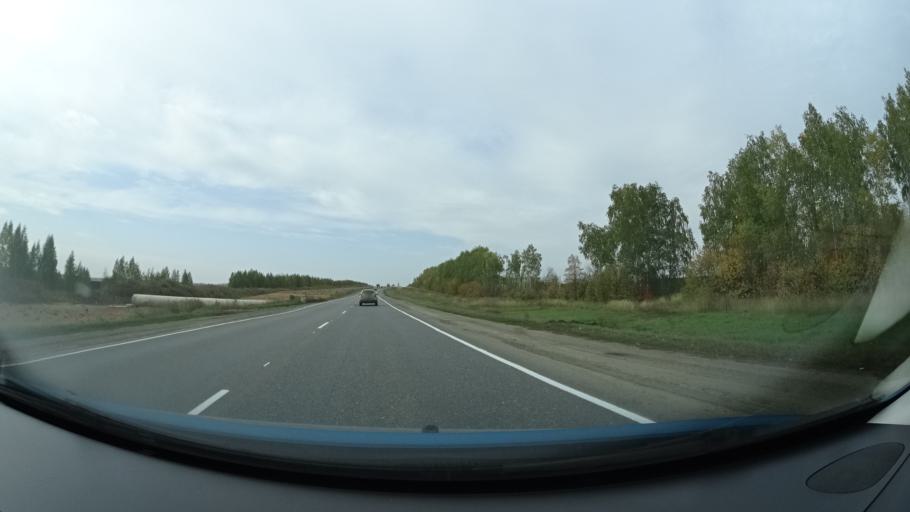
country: RU
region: Bashkortostan
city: Buzdyak
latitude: 54.6557
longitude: 54.6429
